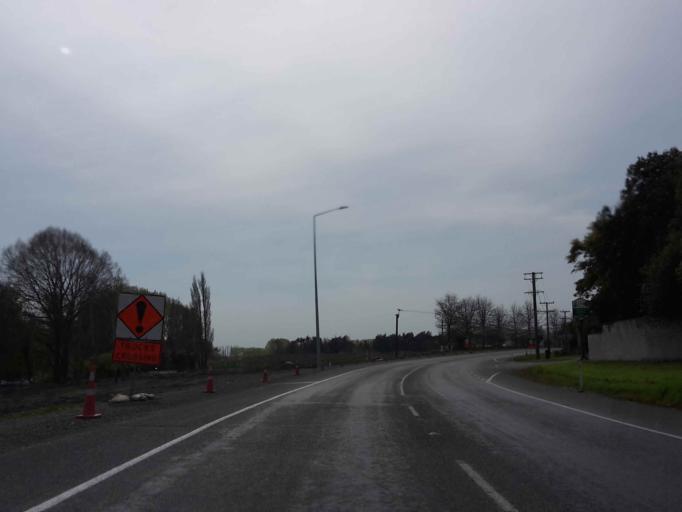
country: NZ
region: Canterbury
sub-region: Waimakariri District
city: Kaiapoi
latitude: -43.4538
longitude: 172.6046
